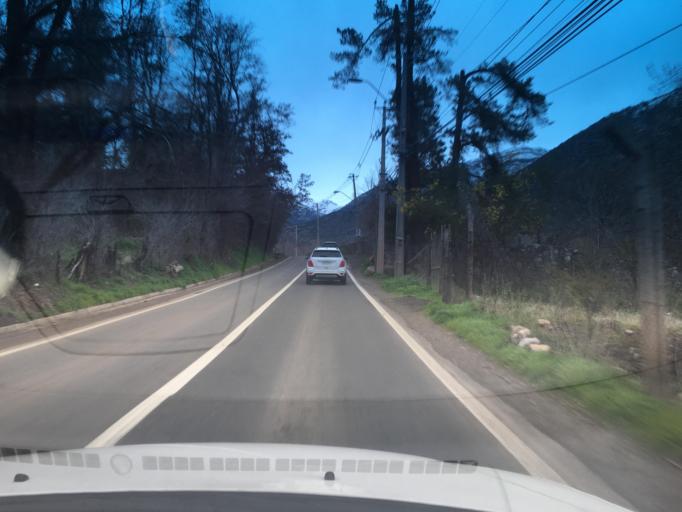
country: CL
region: Santiago Metropolitan
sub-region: Provincia de Cordillera
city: Puente Alto
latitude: -33.6604
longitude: -70.3502
